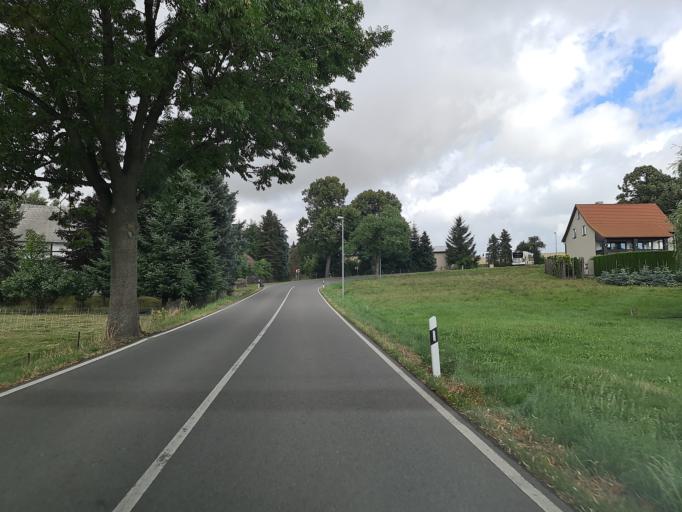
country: DE
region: Saxony
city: Eppendorf
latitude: 50.7812
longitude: 13.2813
